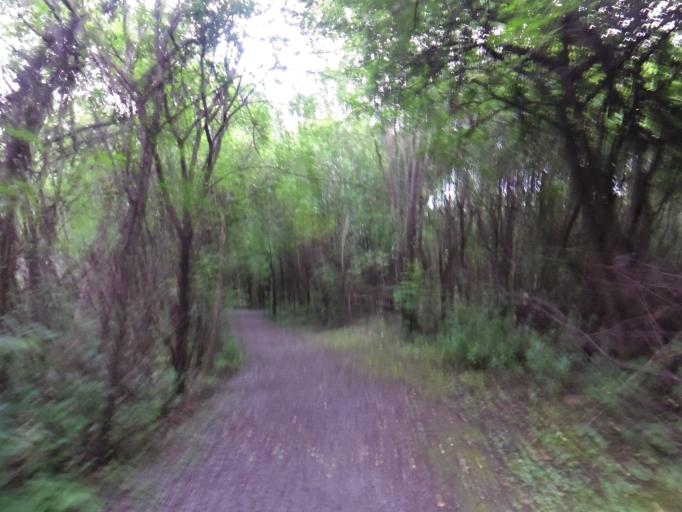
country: CA
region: Ontario
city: Bells Corners
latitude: 45.3601
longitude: -75.8604
